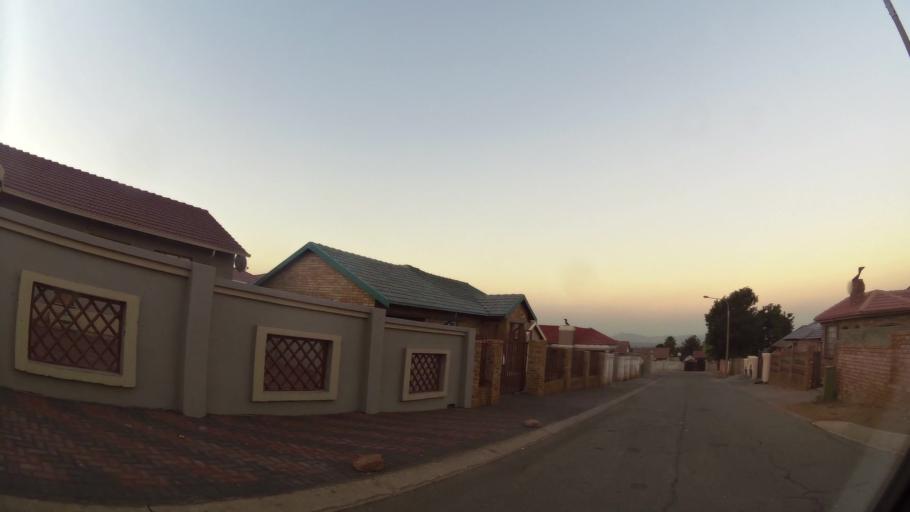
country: ZA
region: North-West
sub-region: Bojanala Platinum District Municipality
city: Rustenburg
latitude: -25.6551
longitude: 27.2036
